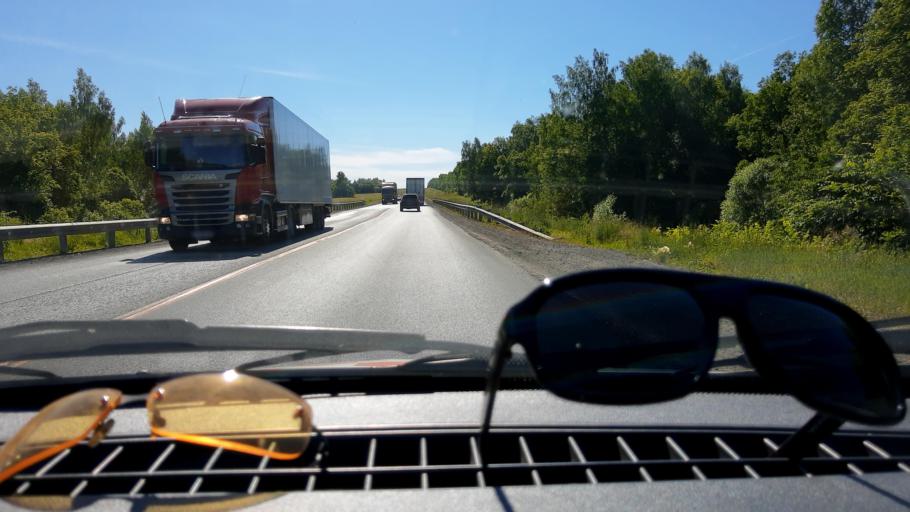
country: RU
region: Bashkortostan
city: Kudeyevskiy
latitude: 54.8127
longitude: 56.6733
